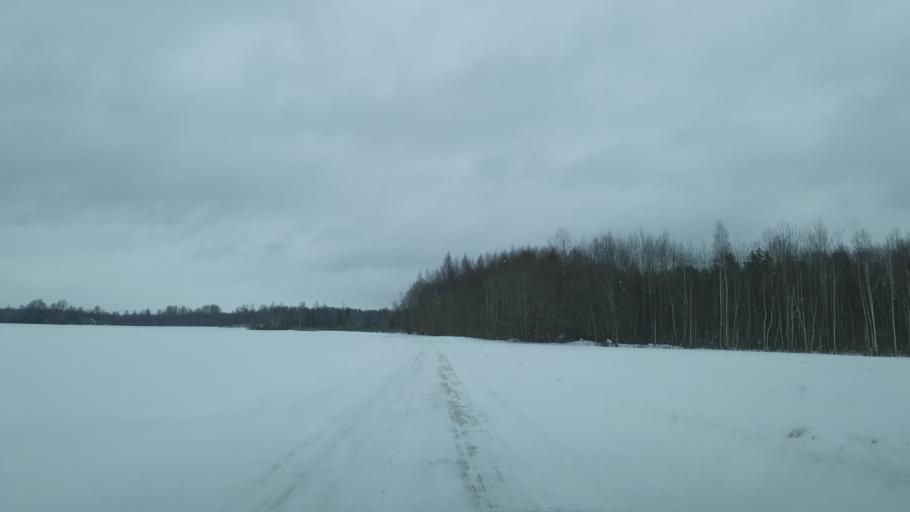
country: EE
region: Polvamaa
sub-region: Raepina vald
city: Rapina
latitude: 58.2031
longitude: 27.2775
